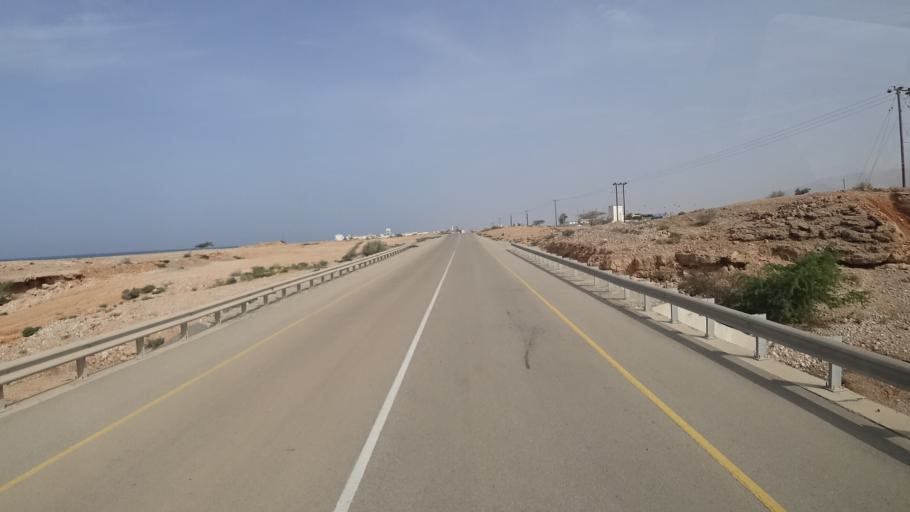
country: OM
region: Ash Sharqiyah
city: Sur
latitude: 22.9965
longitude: 59.1276
